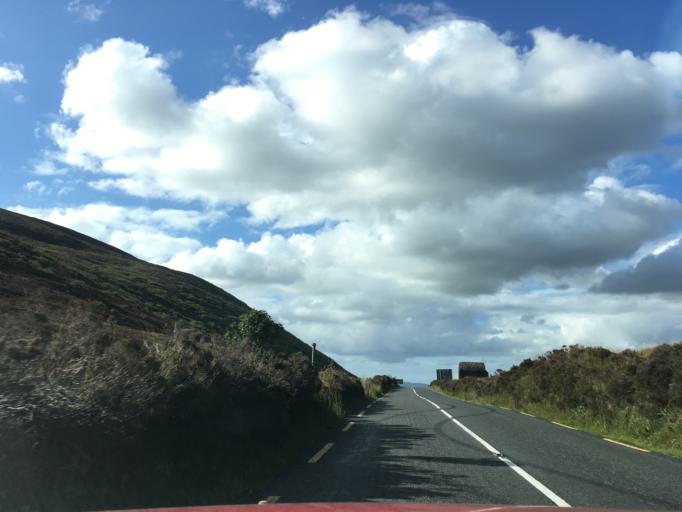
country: IE
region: Munster
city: Cahir
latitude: 52.2403
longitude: -7.9553
